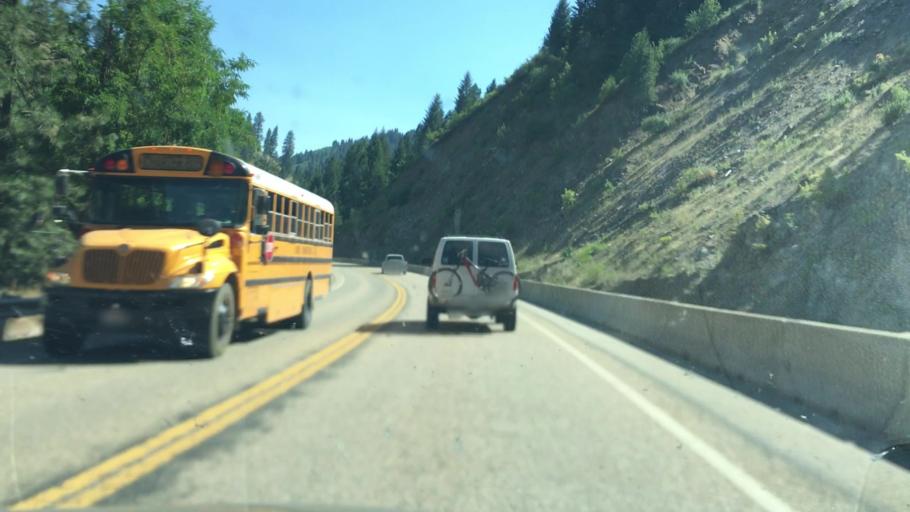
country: US
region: Idaho
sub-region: Valley County
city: Cascade
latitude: 44.1269
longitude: -116.1118
